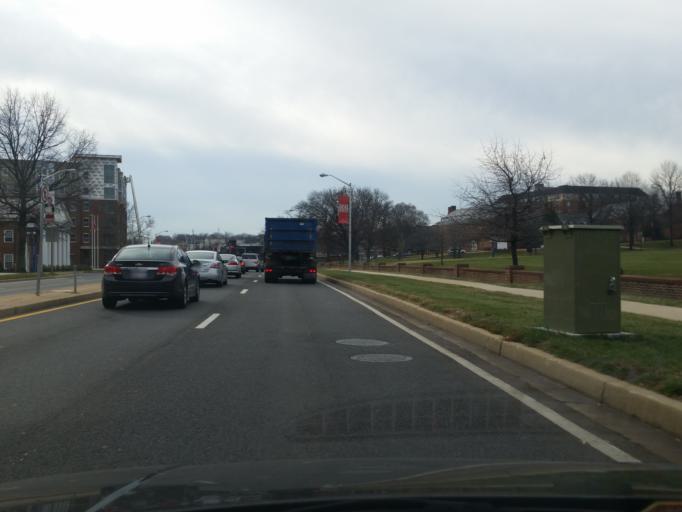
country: US
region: Maryland
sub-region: Prince George's County
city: College Park
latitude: 38.9841
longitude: -76.9378
